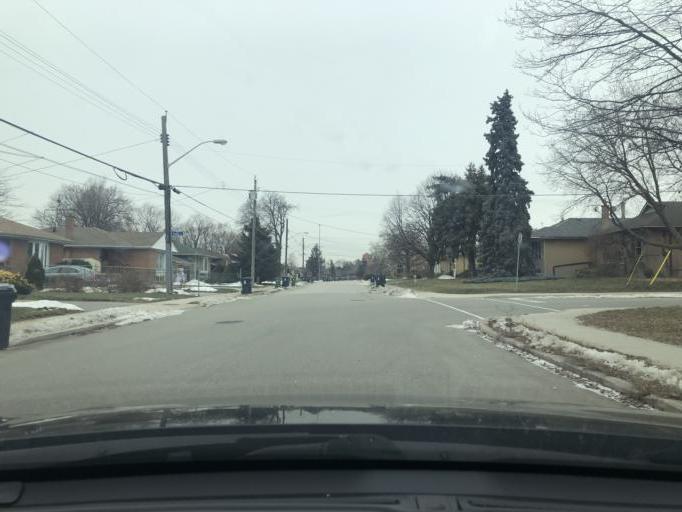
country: CA
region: Ontario
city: Scarborough
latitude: 43.7661
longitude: -79.3071
